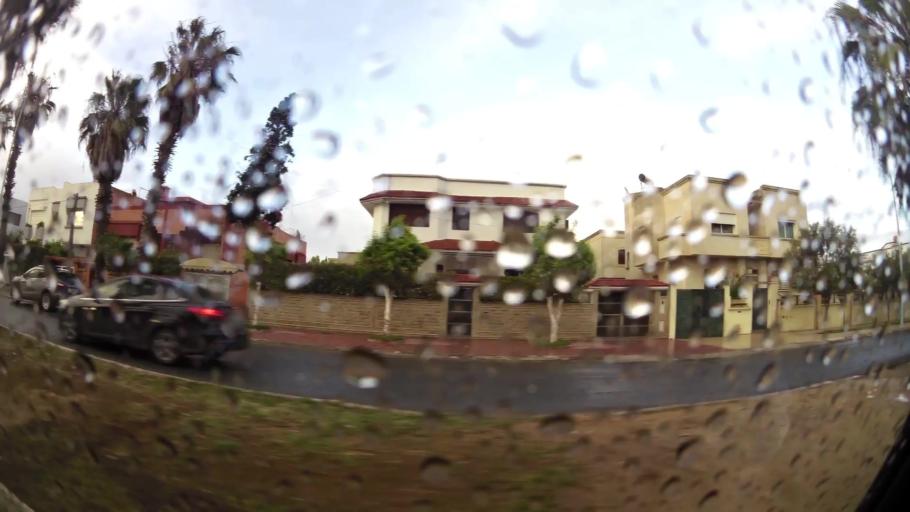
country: MA
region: Doukkala-Abda
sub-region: El-Jadida
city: El Jadida
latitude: 33.2334
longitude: -8.5013
